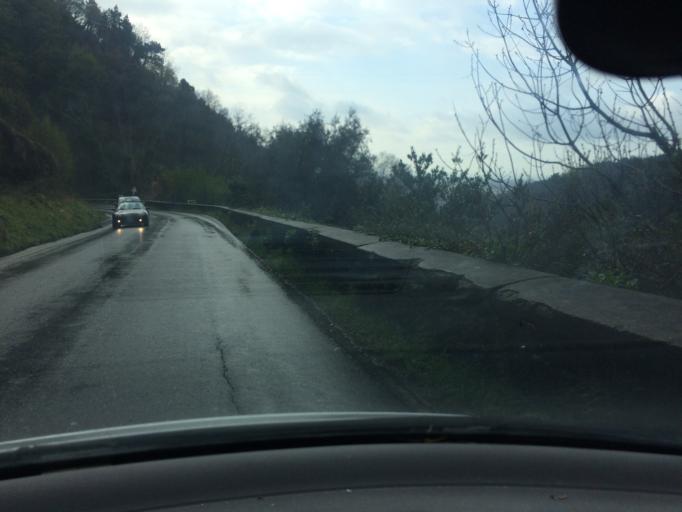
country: IT
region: Tuscany
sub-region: Provincia di Massa-Carrara
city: Massa
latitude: 44.0551
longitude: 10.1237
